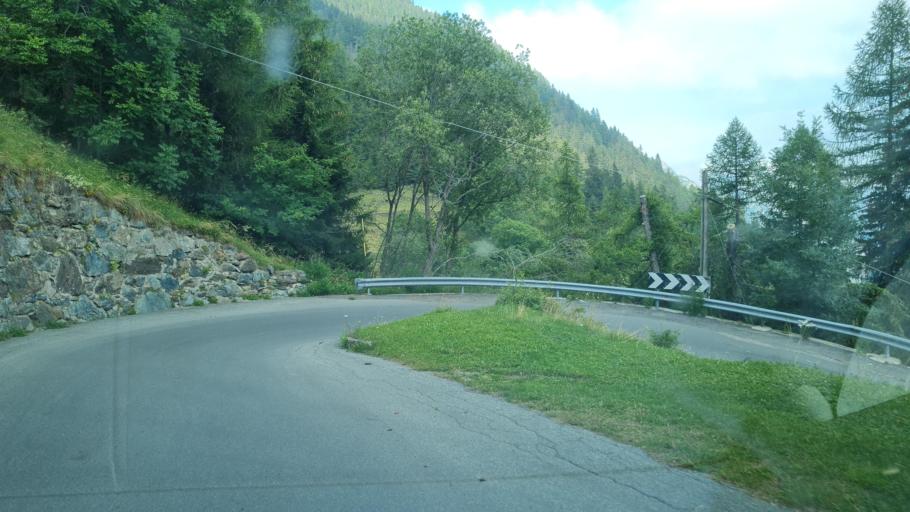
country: IT
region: Aosta Valley
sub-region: Valle d'Aosta
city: Champorcher
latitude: 45.6269
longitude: 7.6166
